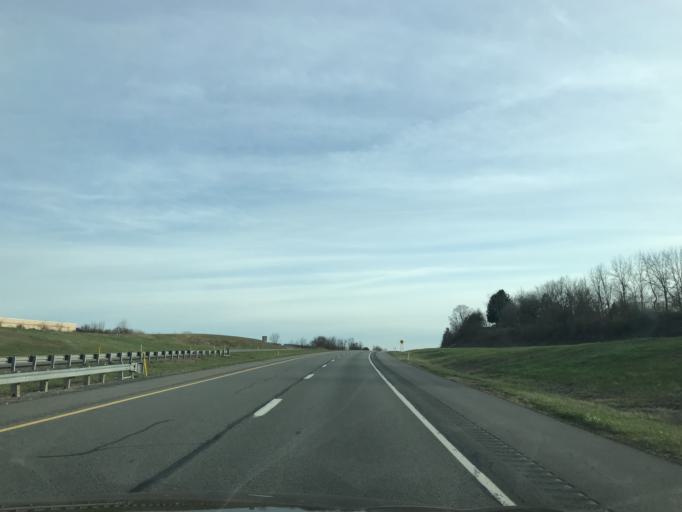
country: US
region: Pennsylvania
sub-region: Northumberland County
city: Milton
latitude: 41.0079
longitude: -76.8306
